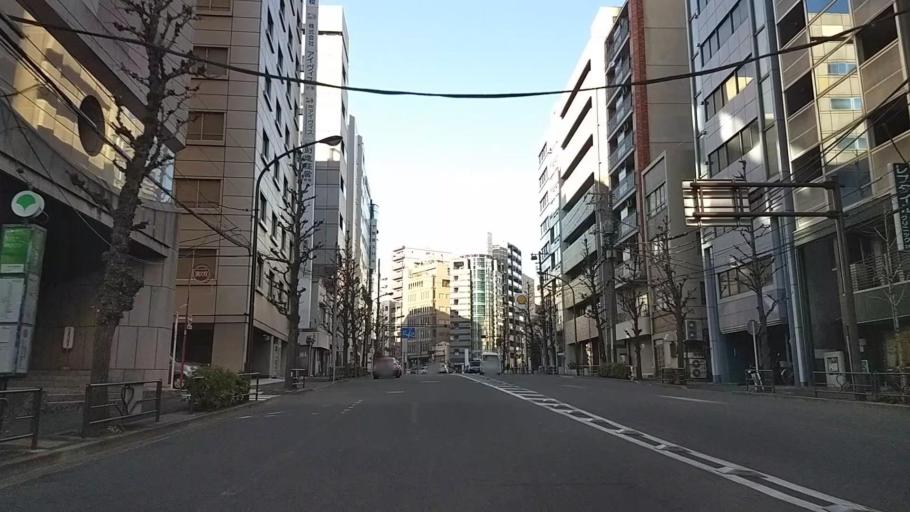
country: JP
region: Tokyo
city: Tokyo
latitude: 35.7030
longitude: 139.7617
